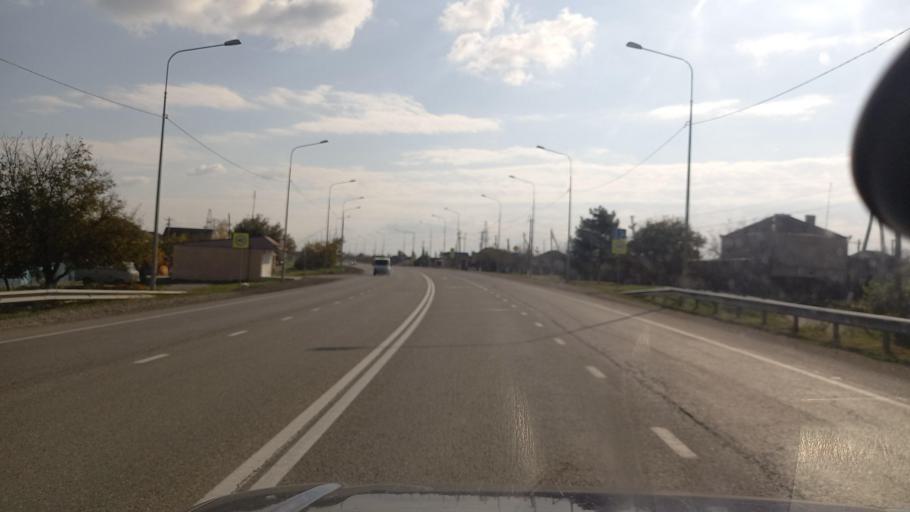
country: RU
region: Krasnodarskiy
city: Novoukrainskiy
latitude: 44.8986
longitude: 38.0418
